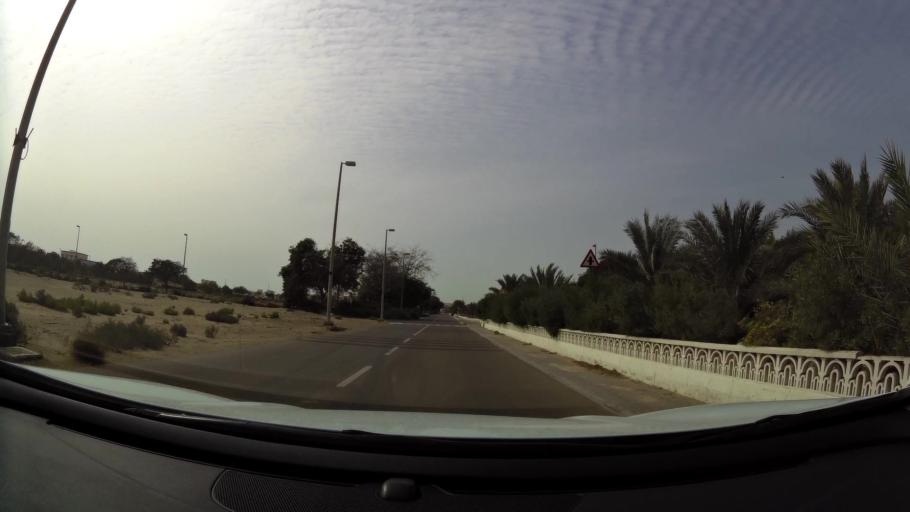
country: AE
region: Abu Dhabi
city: Abu Dhabi
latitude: 24.5762
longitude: 54.6920
